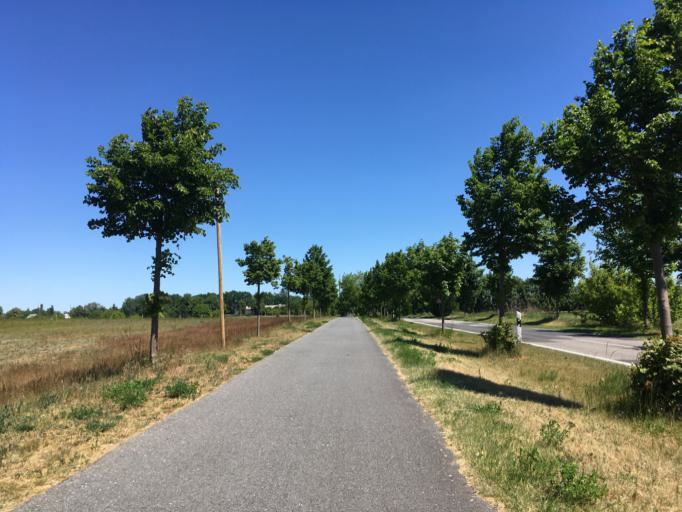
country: DE
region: Brandenburg
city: Zehdenick
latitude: 52.9690
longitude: 13.3144
